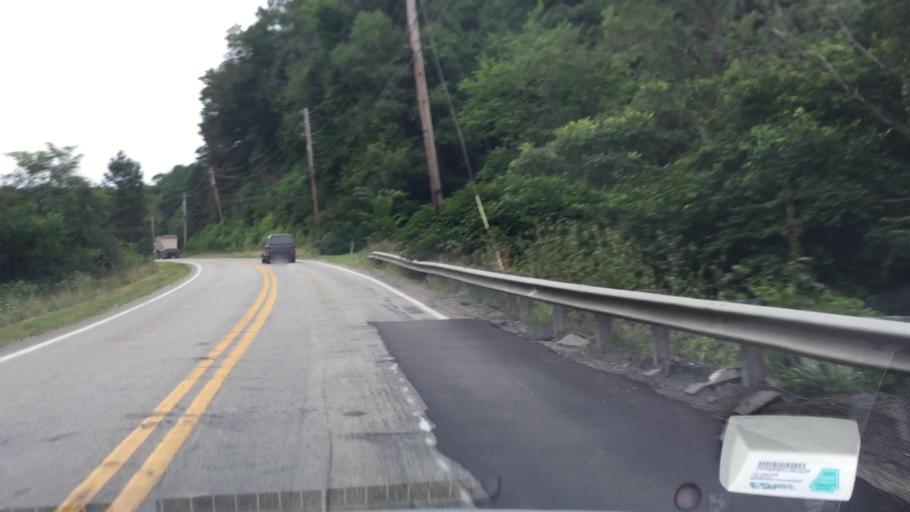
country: US
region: Pennsylvania
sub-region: Allegheny County
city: Curtisville
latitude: 40.6641
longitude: -79.8360
